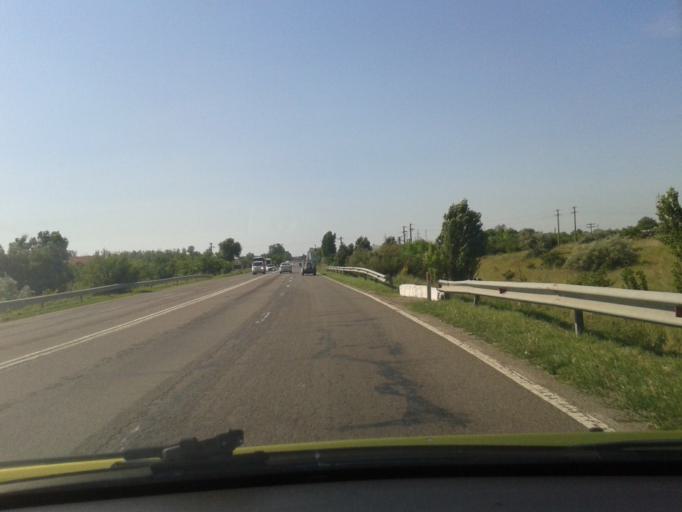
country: RO
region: Constanta
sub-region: Municipiul Mangalia
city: Mangalia
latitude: 43.8378
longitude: 28.5761
